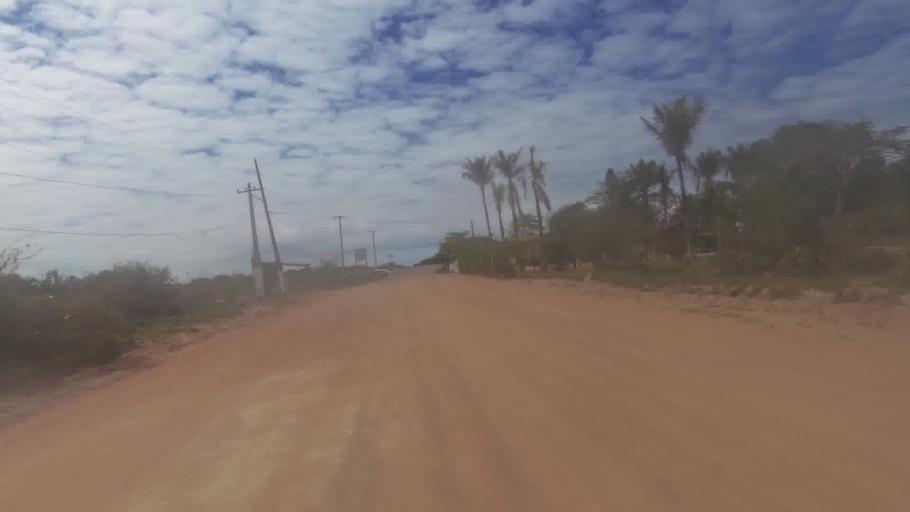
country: BR
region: Espirito Santo
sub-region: Marataizes
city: Marataizes
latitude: -21.2343
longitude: -40.9775
